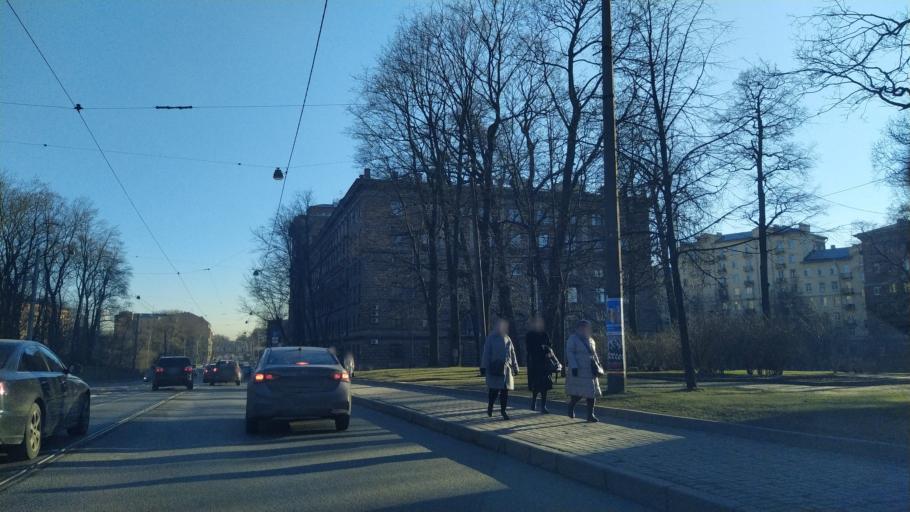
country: RU
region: Leningrad
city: Svetlanovskiy
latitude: 59.9968
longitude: 30.3302
